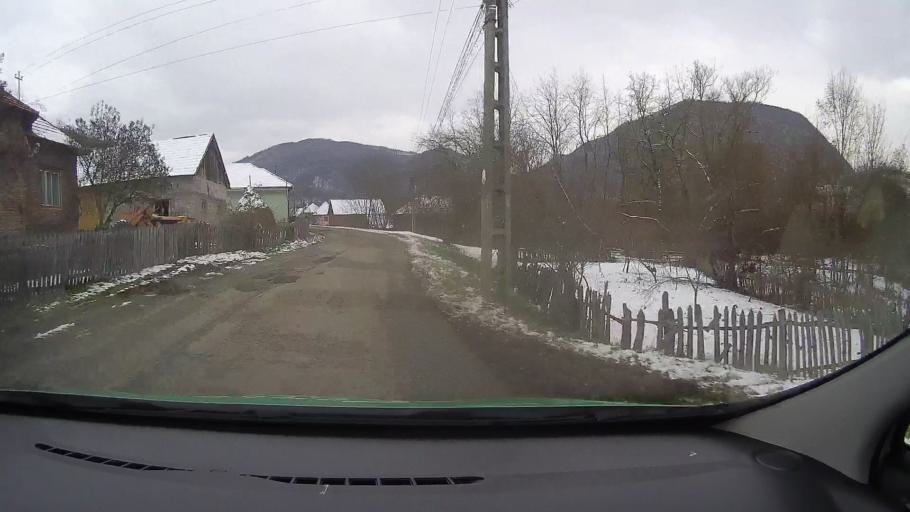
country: RO
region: Hunedoara
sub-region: Comuna Balsa
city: Balsa
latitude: 46.0242
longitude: 23.1144
